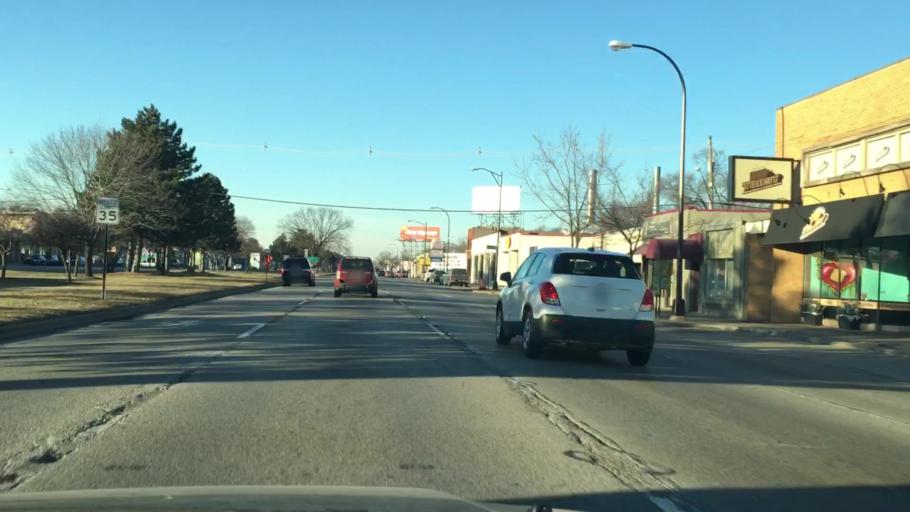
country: US
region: Michigan
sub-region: Oakland County
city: Ferndale
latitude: 42.4638
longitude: -83.1366
